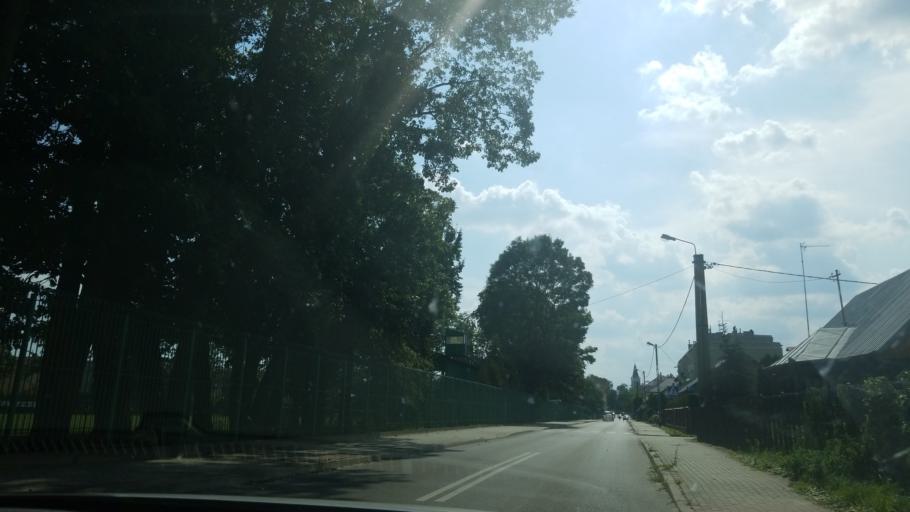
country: PL
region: Subcarpathian Voivodeship
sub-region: Powiat nizanski
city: Nisko
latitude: 50.5223
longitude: 22.1475
